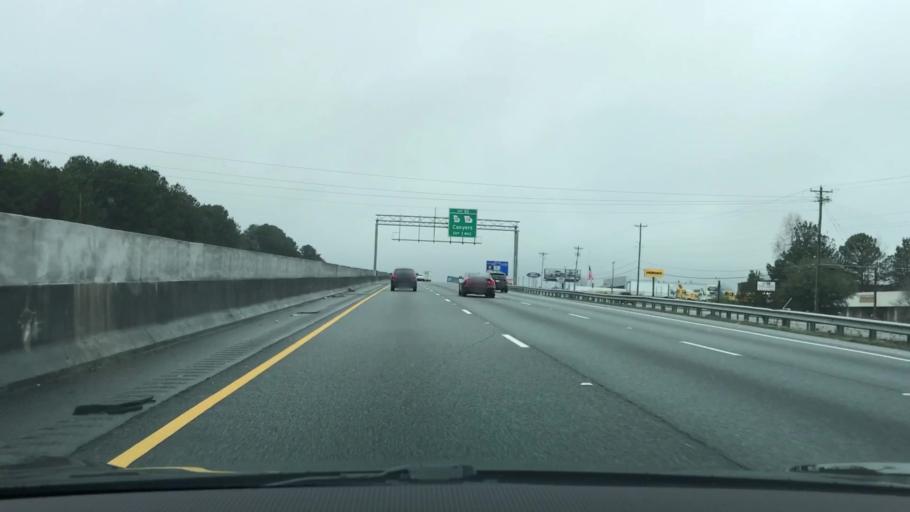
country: US
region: Georgia
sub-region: Rockdale County
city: Conyers
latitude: 33.6430
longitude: -83.9887
